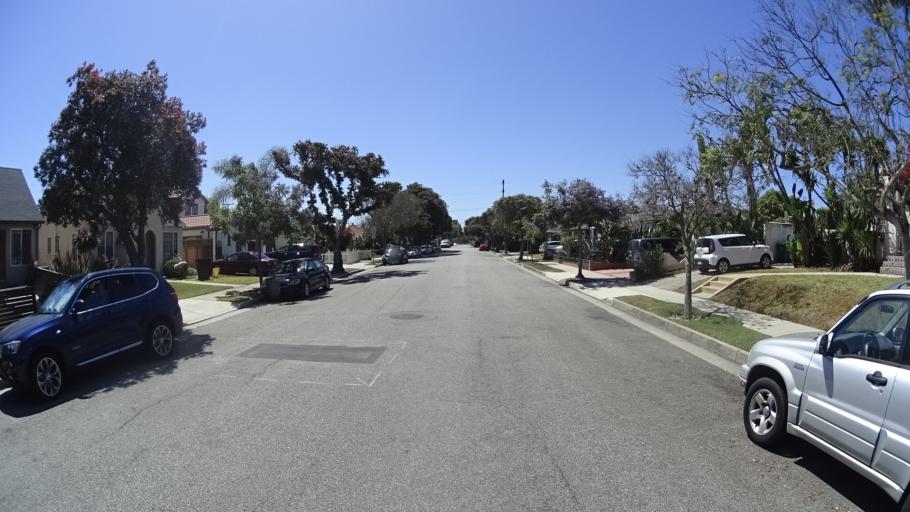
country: US
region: California
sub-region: Los Angeles County
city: Santa Monica
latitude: 34.0241
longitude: -118.4560
